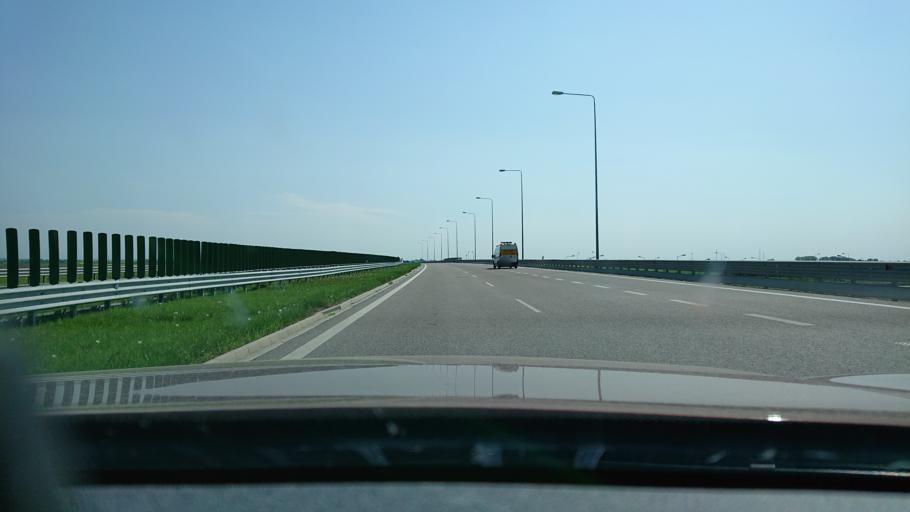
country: PL
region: Subcarpathian Voivodeship
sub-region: Powiat jaroslawski
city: Radymno
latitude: 49.9106
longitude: 22.8152
